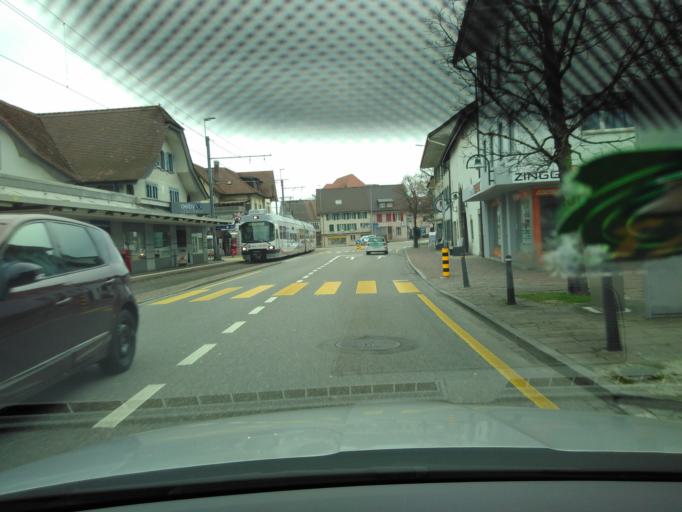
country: CH
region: Aargau
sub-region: Bezirk Aarau
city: Oberentfelden
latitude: 47.3560
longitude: 8.0466
